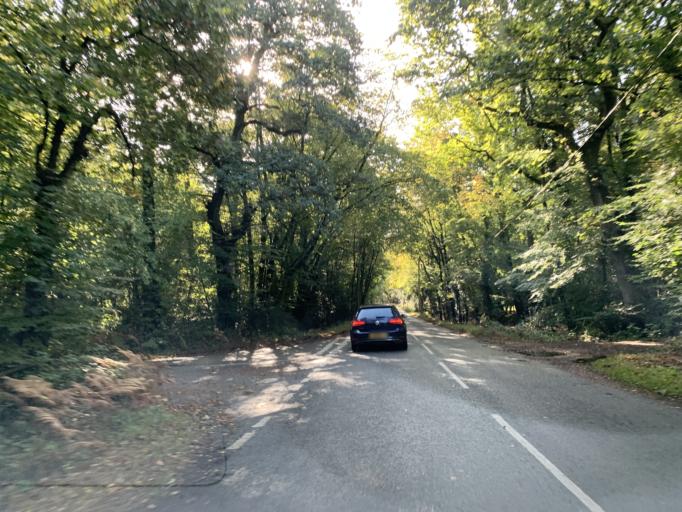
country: GB
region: England
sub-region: Wiltshire
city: Downton
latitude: 50.9656
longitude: -1.7039
